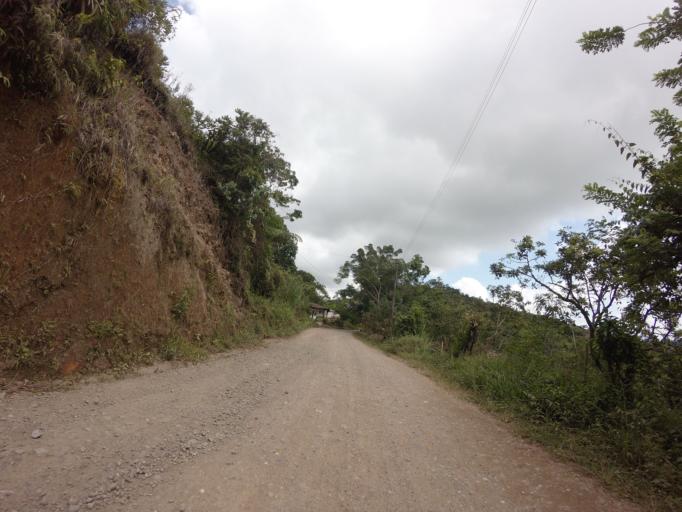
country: CO
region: Caldas
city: Victoria
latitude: 5.3063
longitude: -74.9805
